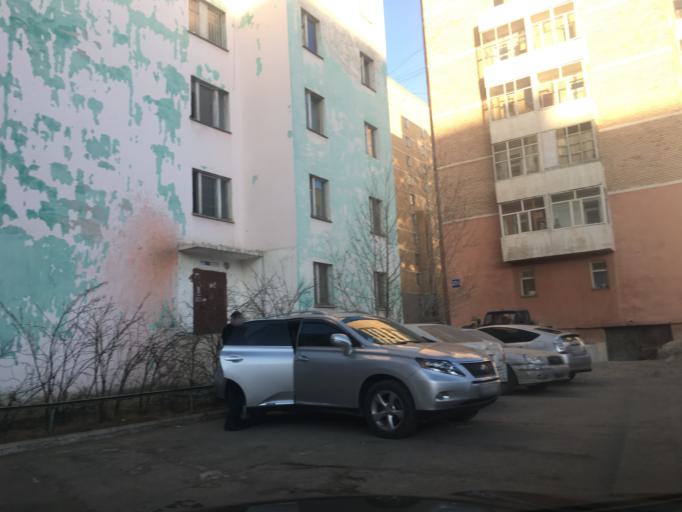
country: MN
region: Ulaanbaatar
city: Ulaanbaatar
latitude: 47.9203
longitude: 106.8822
